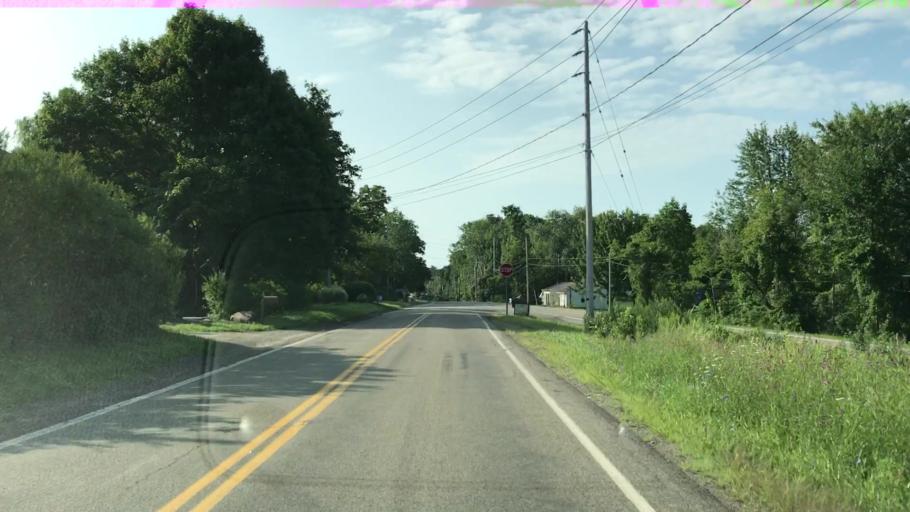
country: US
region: New York
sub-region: Chautauqua County
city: Mayville
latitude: 42.2594
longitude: -79.4690
